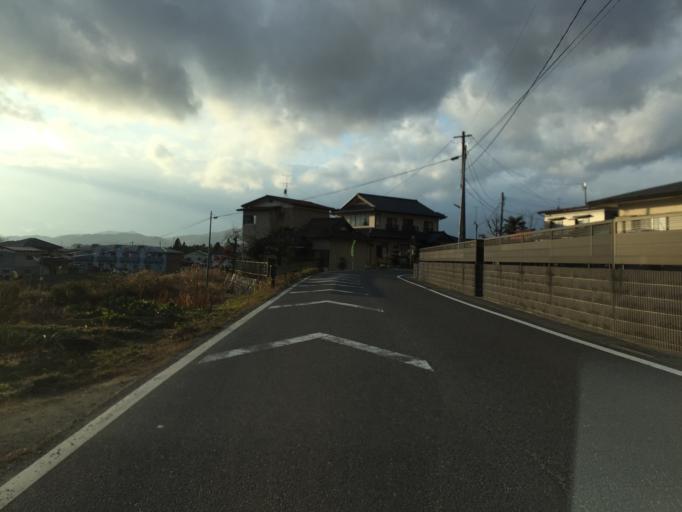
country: JP
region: Fukushima
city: Motomiya
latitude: 37.5068
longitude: 140.4123
